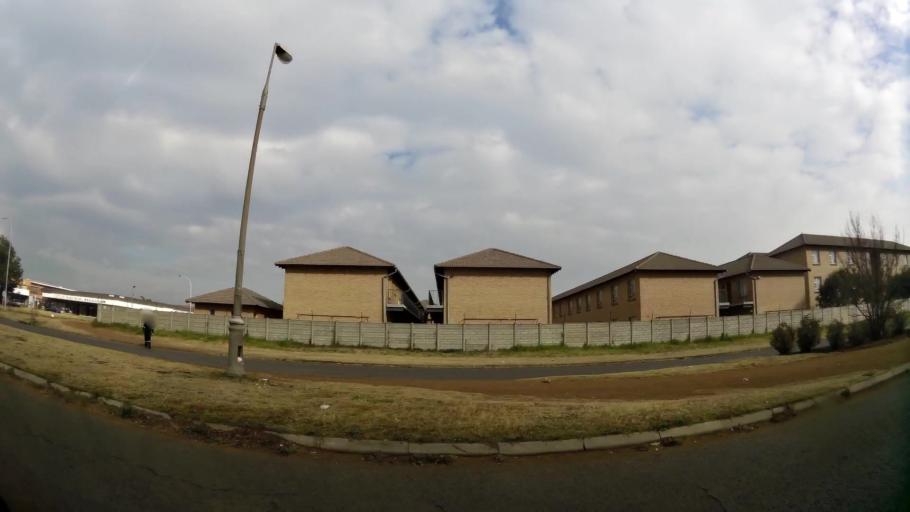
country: ZA
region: Gauteng
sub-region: Sedibeng District Municipality
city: Vanderbijlpark
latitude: -26.6949
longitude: 27.8403
